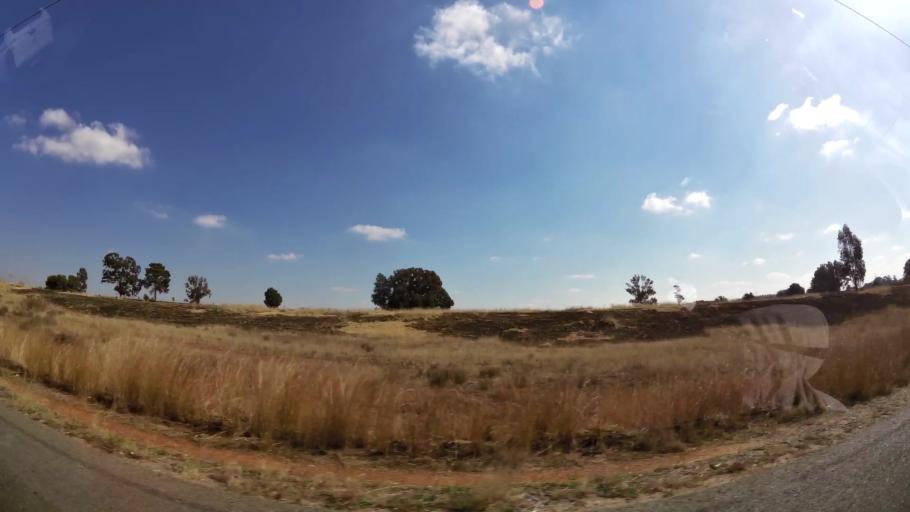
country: ZA
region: Gauteng
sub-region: West Rand District Municipality
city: Randfontein
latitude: -26.1581
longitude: 27.7621
